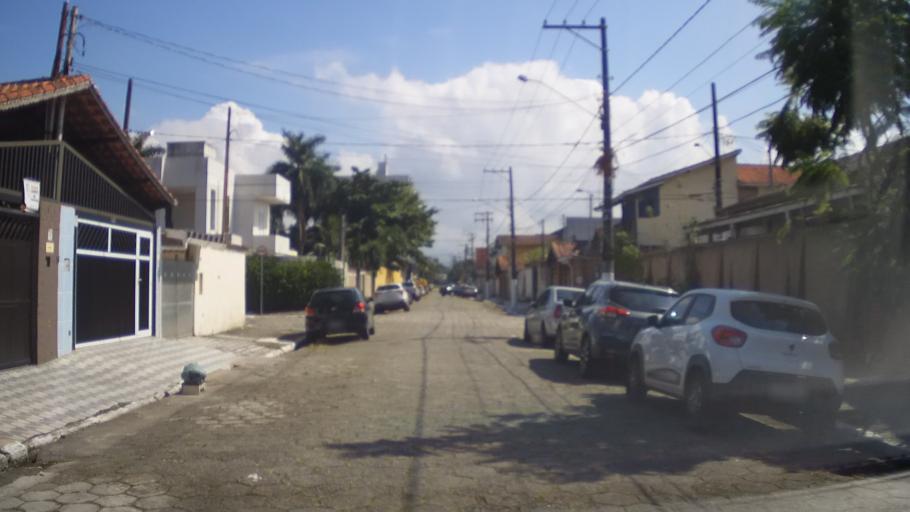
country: BR
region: Sao Paulo
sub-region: Praia Grande
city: Praia Grande
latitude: -24.0054
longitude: -46.4201
